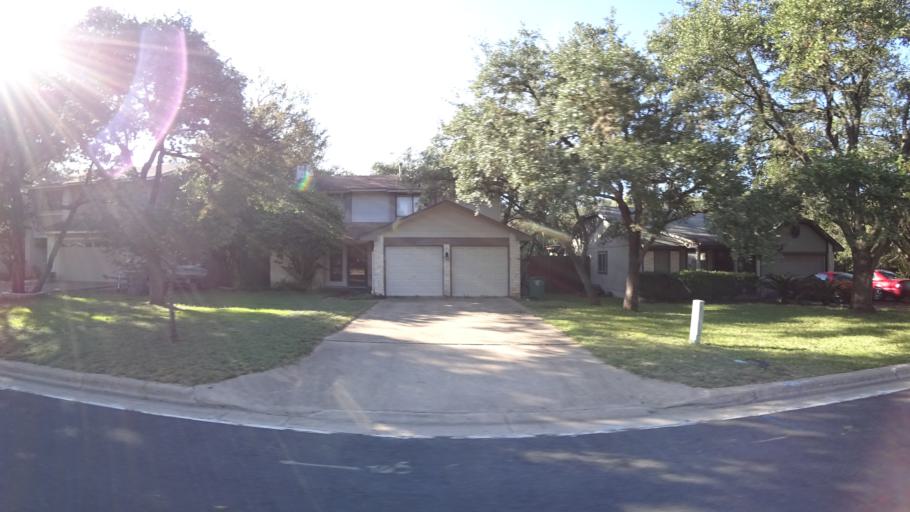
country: US
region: Texas
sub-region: Travis County
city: Shady Hollow
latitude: 30.2078
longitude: -97.8450
